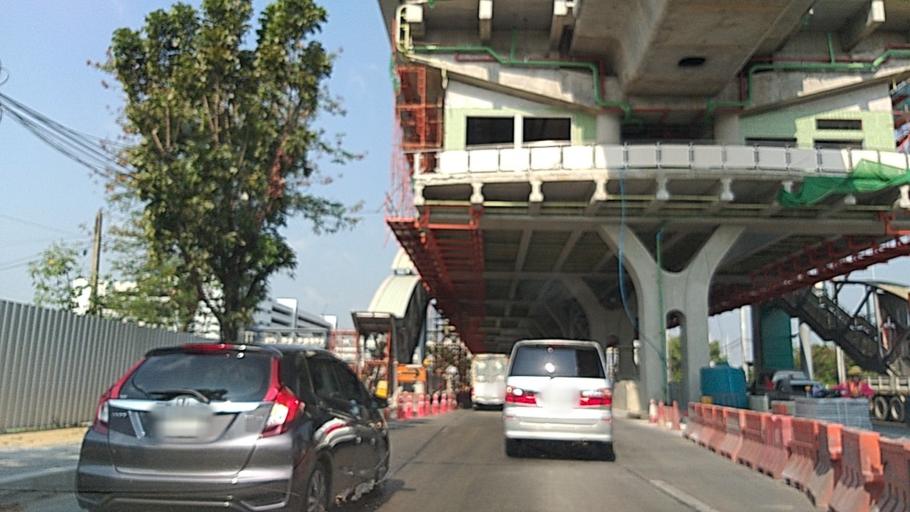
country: TH
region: Bangkok
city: Sai Mai
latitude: 13.9323
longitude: 100.6474
